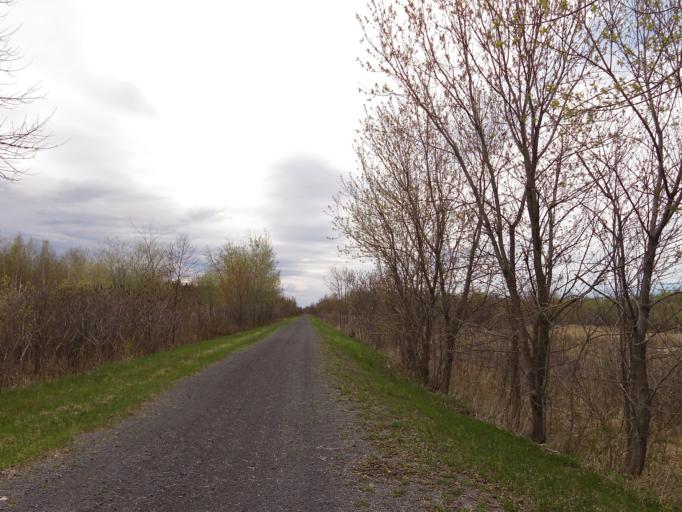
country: CA
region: Ontario
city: Hawkesbury
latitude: 45.5438
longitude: -74.7676
